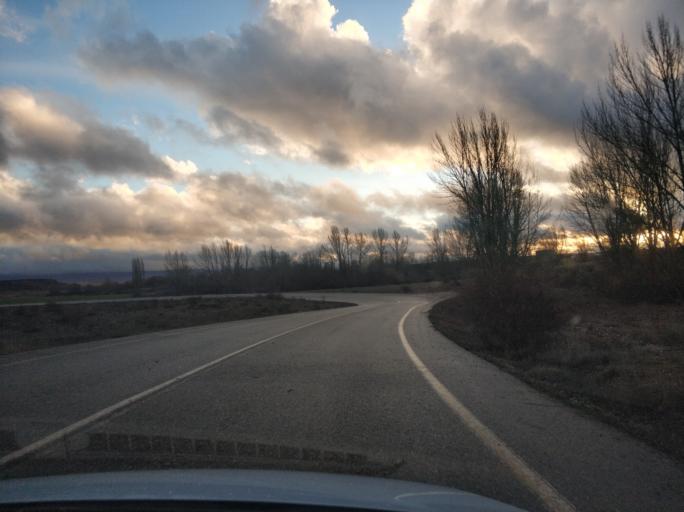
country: ES
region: Castille and Leon
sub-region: Provincia de Segovia
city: Ayllon
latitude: 41.4140
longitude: -3.4080
